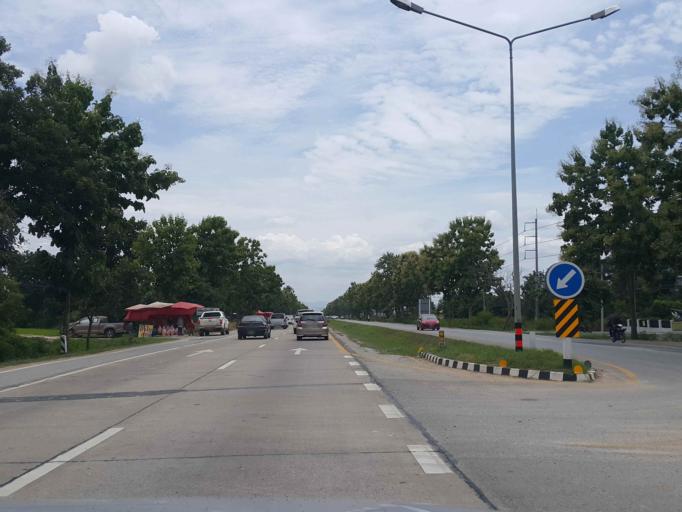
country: TH
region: Chiang Mai
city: Saraphi
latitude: 18.6887
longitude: 99.0500
